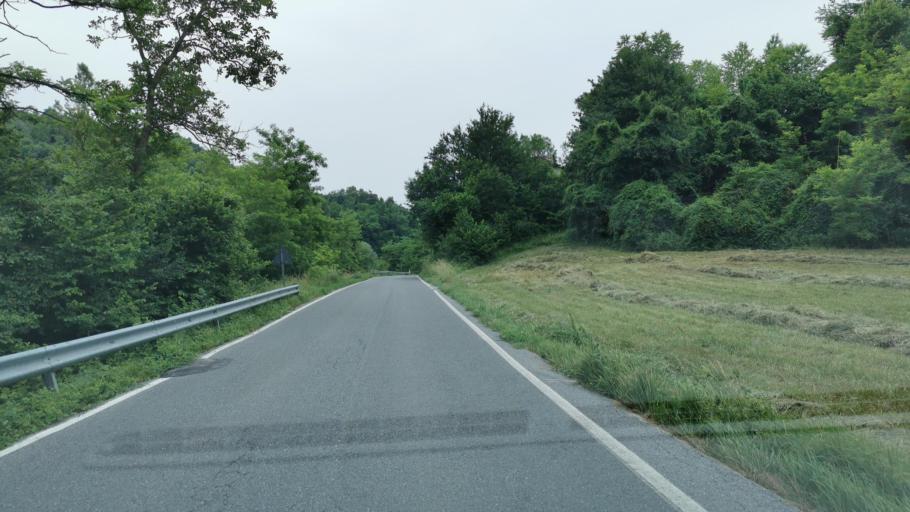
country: IT
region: Piedmont
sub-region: Provincia di Cuneo
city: Ceva
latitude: 44.4012
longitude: 8.0479
